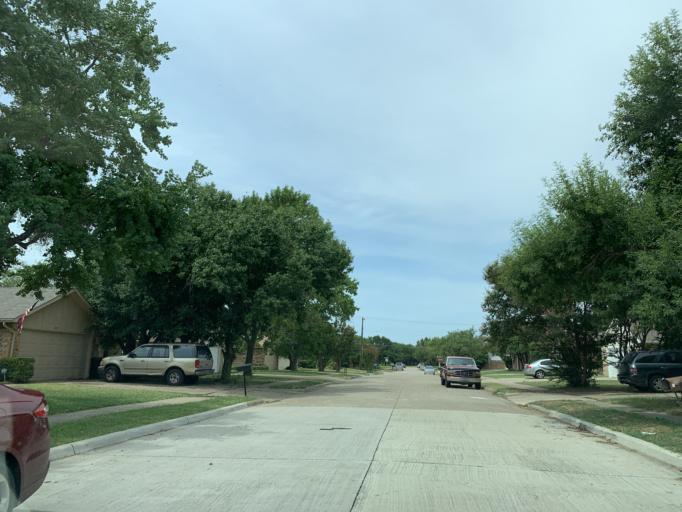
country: US
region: Texas
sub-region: Dallas County
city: Cedar Hill
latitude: 32.6526
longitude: -97.0266
